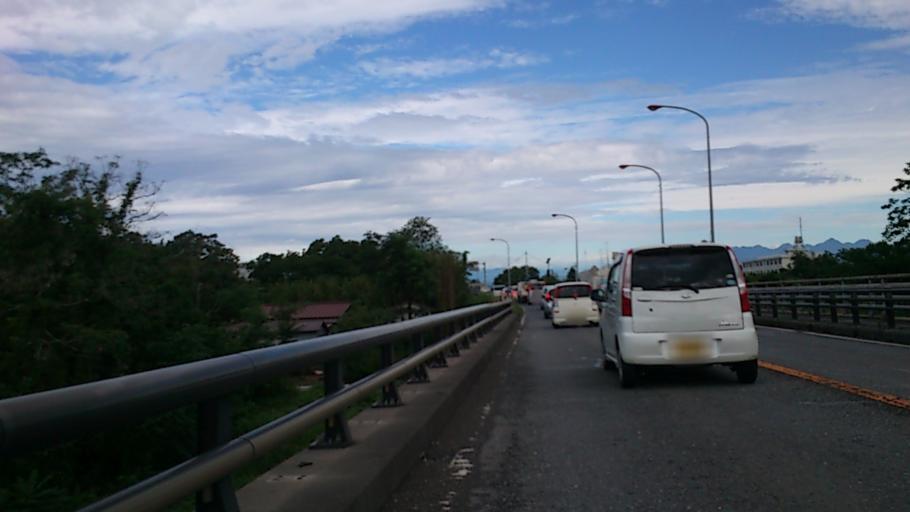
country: JP
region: Gunma
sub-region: Sawa-gun
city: Tamamura
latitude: 36.2684
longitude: 139.1195
